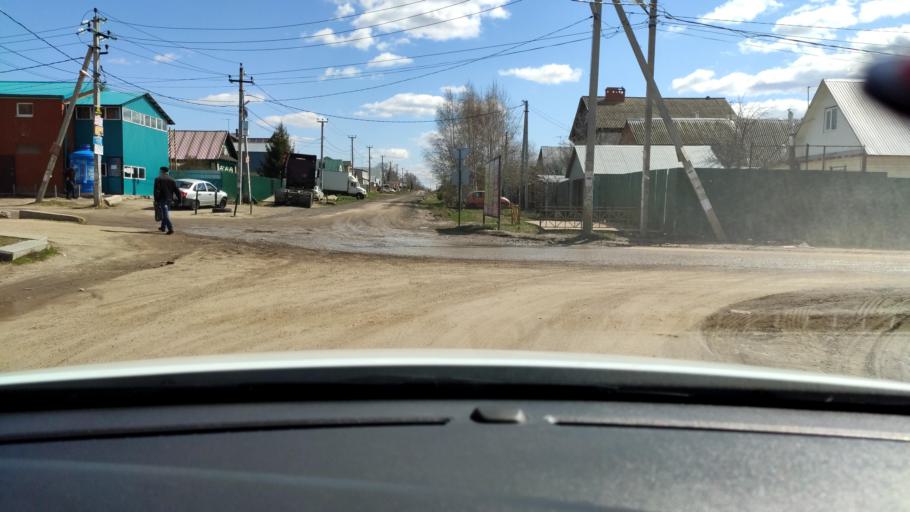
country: RU
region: Tatarstan
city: Stolbishchi
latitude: 55.7176
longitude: 49.3540
